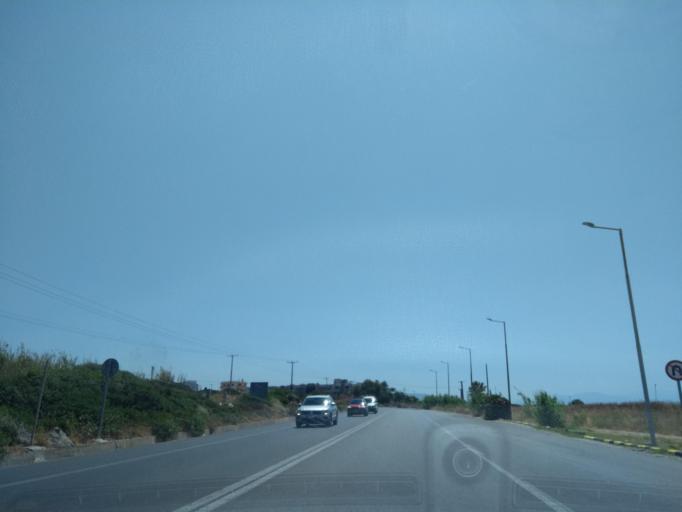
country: GR
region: Crete
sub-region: Nomos Rethymnis
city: Panormos
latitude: 35.4030
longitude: 24.6309
